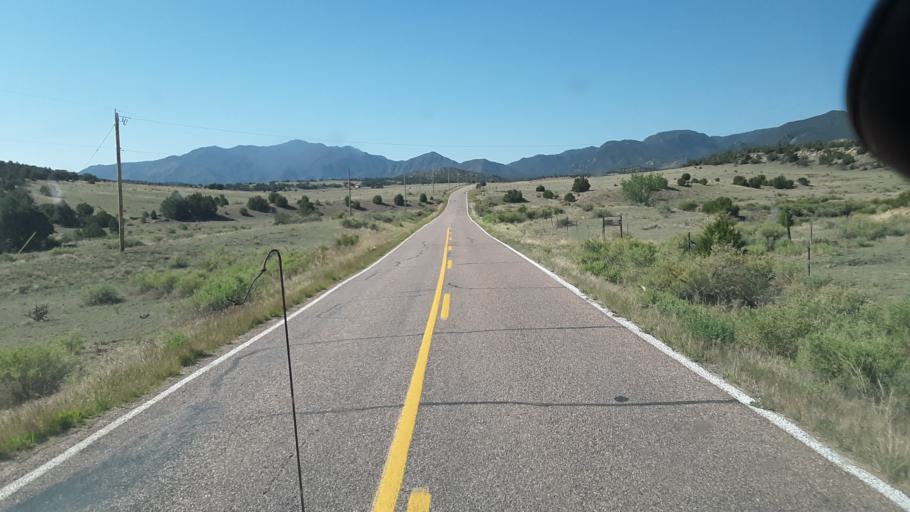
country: US
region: Colorado
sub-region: Fremont County
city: Canon City
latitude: 38.4696
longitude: -105.3781
